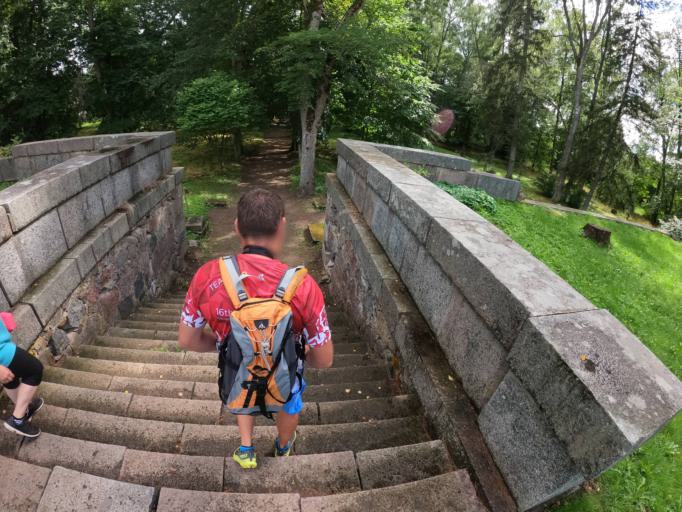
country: LV
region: Aizpute
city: Aizpute
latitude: 56.7350
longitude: 21.7302
